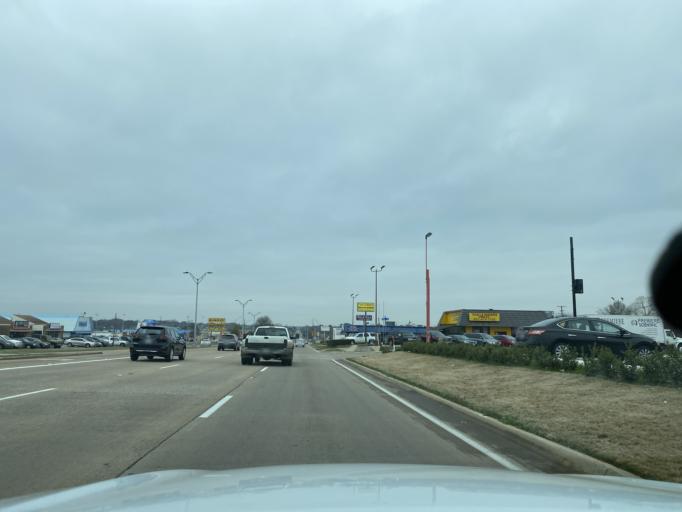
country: US
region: Texas
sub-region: Tarrant County
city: Arlington
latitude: 32.7081
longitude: -97.0936
